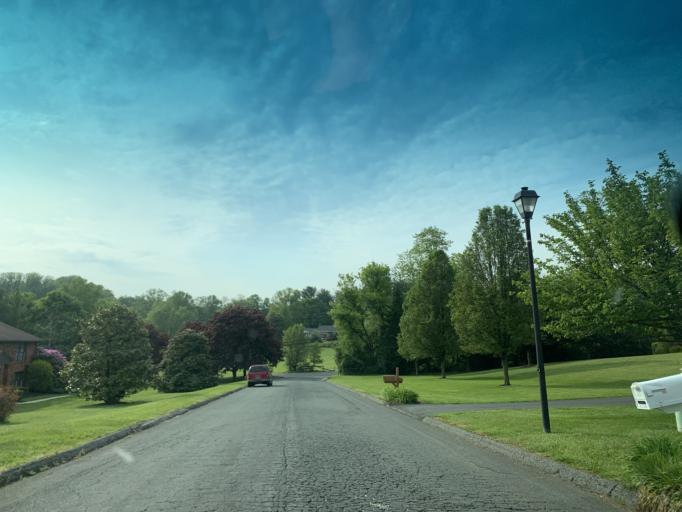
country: US
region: Maryland
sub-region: Baltimore County
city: Kingsville
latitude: 39.4658
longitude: -76.4439
